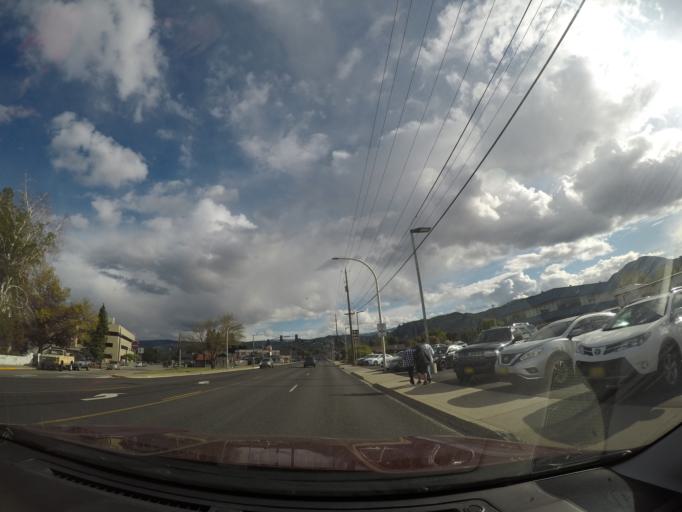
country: US
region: Washington
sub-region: Chelan County
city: Wenatchee
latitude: 47.4343
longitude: -120.3249
